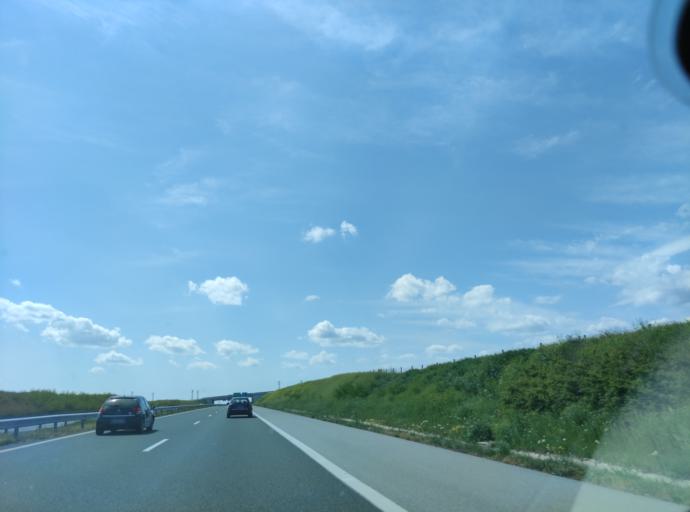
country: BG
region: Yambol
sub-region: Obshtina Straldzha
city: Straldzha
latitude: 42.5565
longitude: 26.5847
